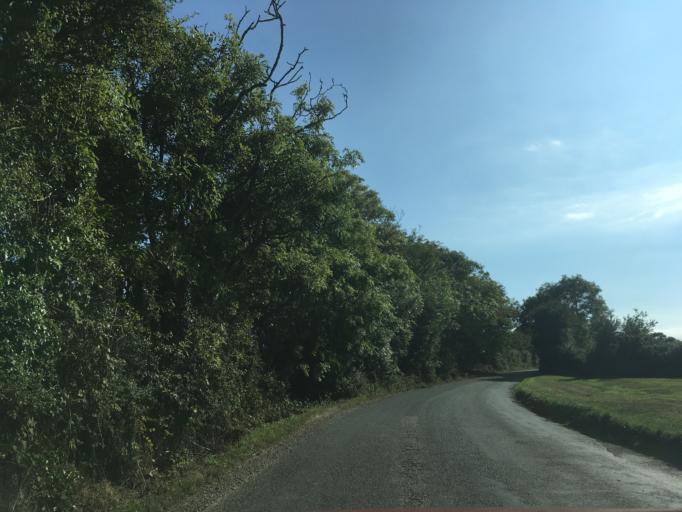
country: IE
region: Leinster
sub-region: Loch Garman
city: Rosslare
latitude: 52.2419
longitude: -6.3965
